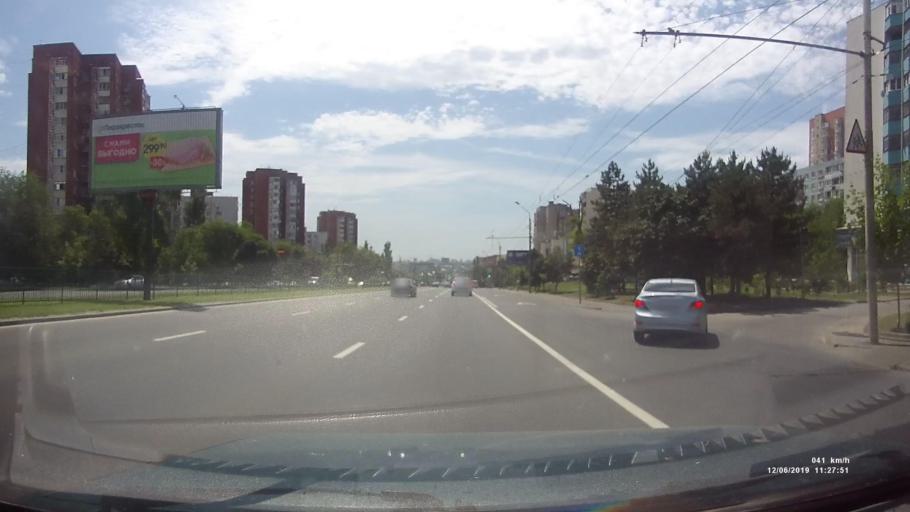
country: RU
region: Rostov
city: Severnyy
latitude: 47.2932
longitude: 39.7136
